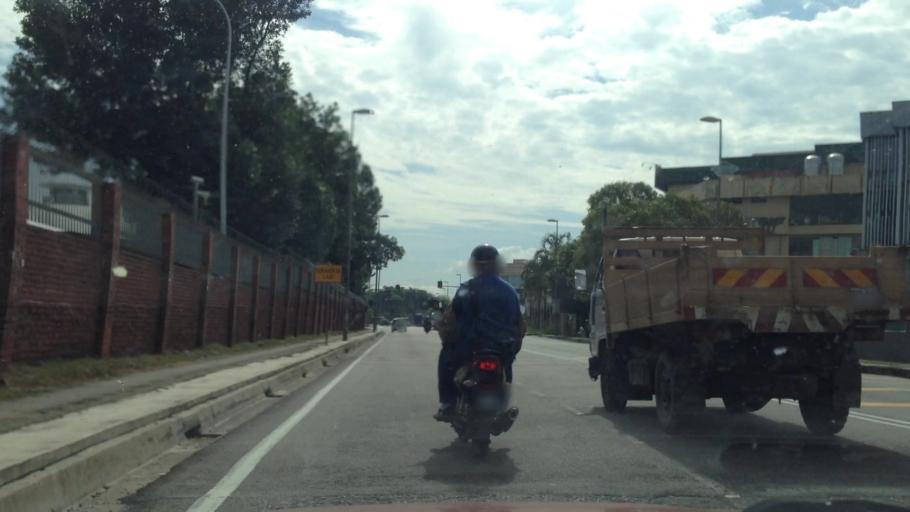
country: MY
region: Selangor
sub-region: Petaling
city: Petaling Jaya
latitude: 3.0827
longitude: 101.6210
